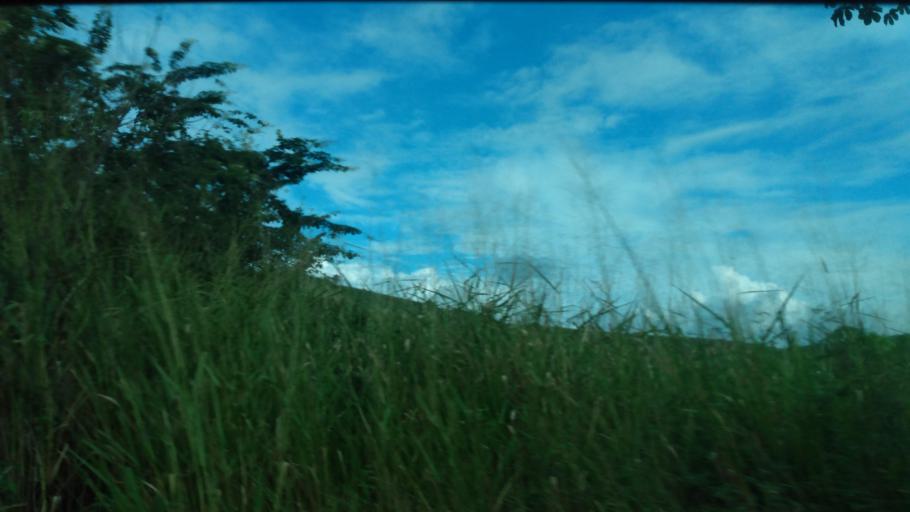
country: BR
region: Pernambuco
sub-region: Catende
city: Catende
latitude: -8.6894
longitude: -35.7071
